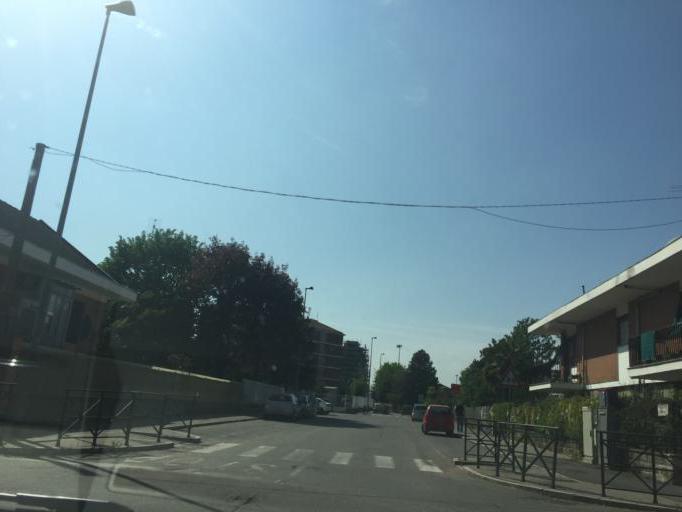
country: IT
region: Piedmont
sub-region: Provincia di Torino
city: Lesna
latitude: 45.0569
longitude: 7.6223
